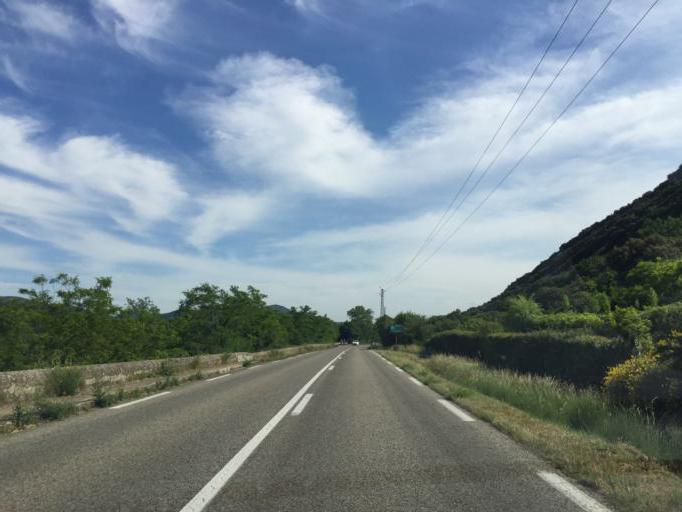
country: FR
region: Rhone-Alpes
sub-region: Departement de l'Ardeche
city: Cruas
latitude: 44.6797
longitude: 4.7715
